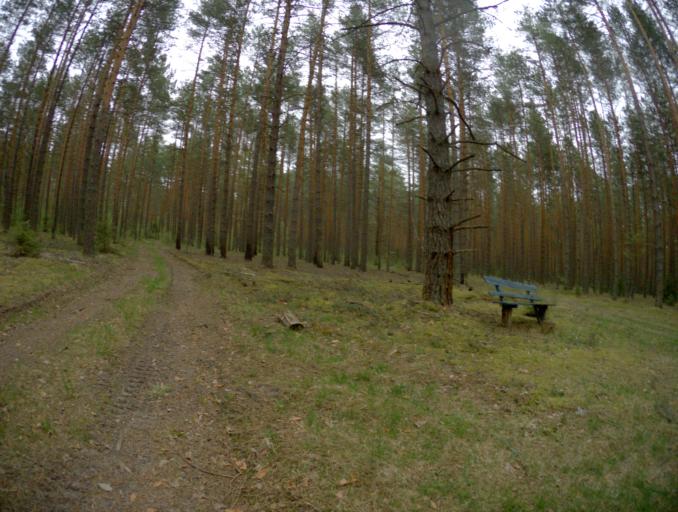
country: RU
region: Vladimir
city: Golovino
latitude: 55.9096
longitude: 40.4472
